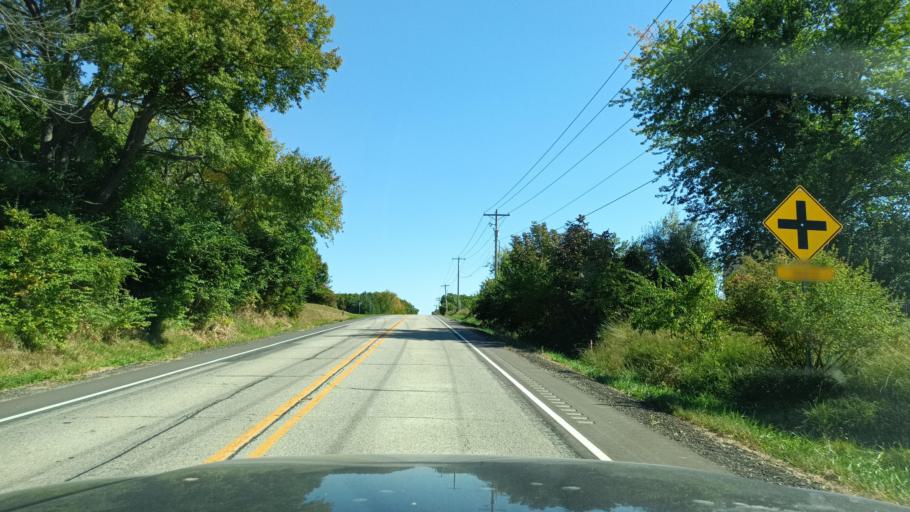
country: US
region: Illinois
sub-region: McLean County
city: Danvers
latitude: 40.6169
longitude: -89.2222
